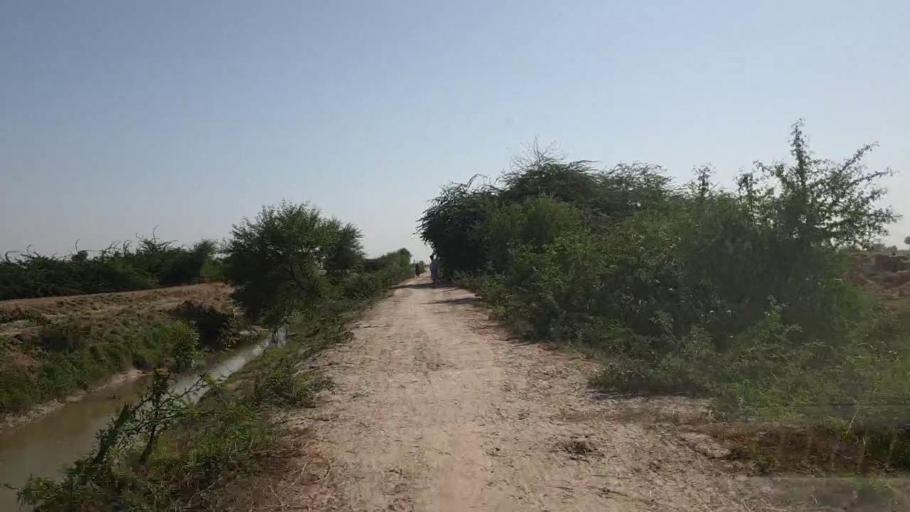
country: PK
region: Sindh
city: Kadhan
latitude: 24.6167
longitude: 68.9973
